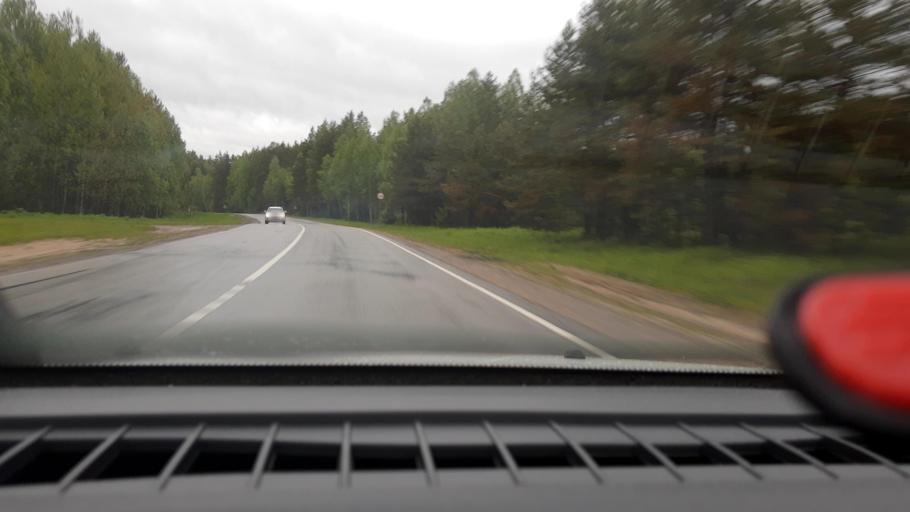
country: RU
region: Nizjnij Novgorod
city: Krasnyye Baki
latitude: 56.9848
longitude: 45.1177
